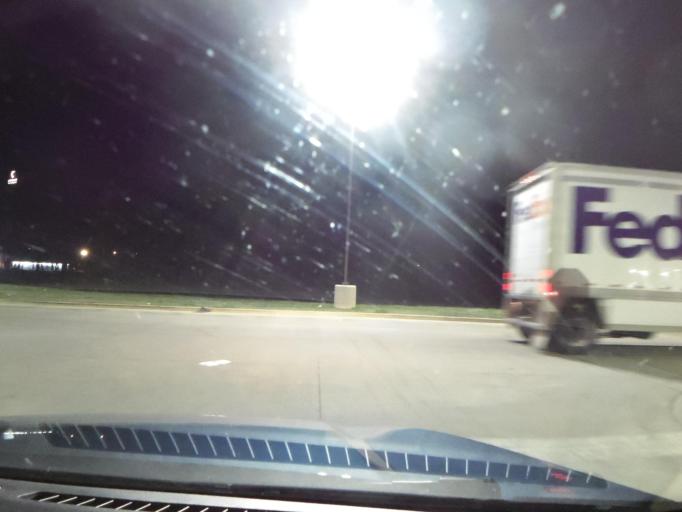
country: US
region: Illinois
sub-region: Johnson County
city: Goreville
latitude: 37.6196
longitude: -88.9849
